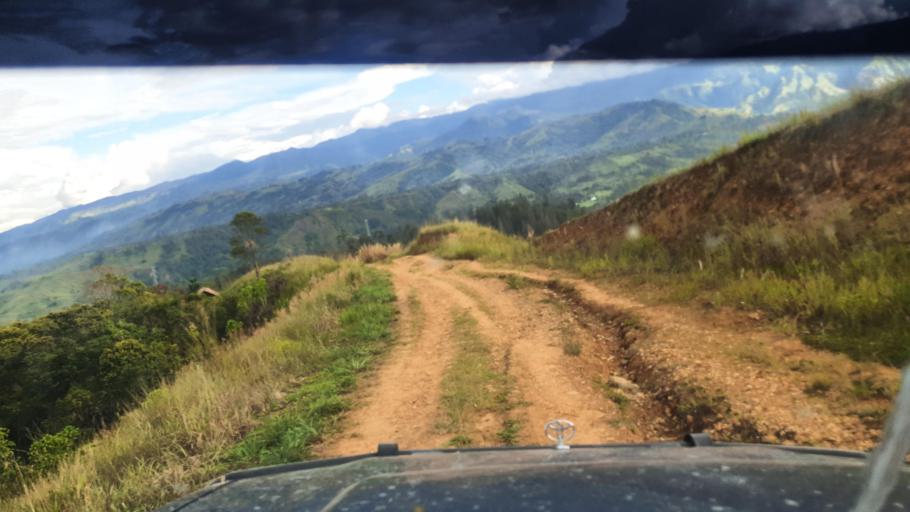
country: PG
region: Jiwaka
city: Minj
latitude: -5.9321
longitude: 144.8193
